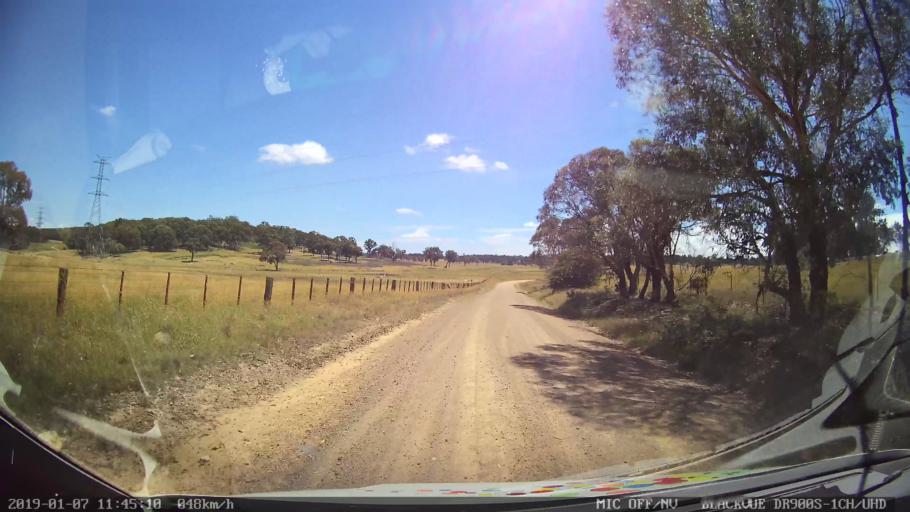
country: AU
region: New South Wales
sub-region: Guyra
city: Guyra
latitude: -30.3480
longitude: 151.6052
